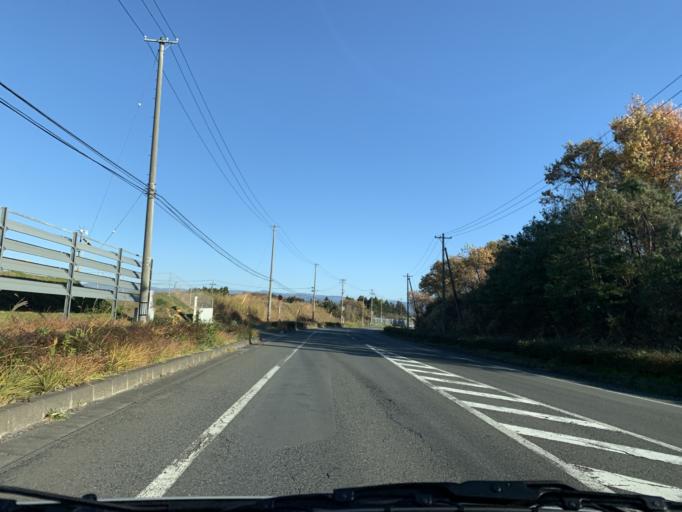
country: JP
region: Iwate
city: Kitakami
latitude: 39.2383
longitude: 141.0899
